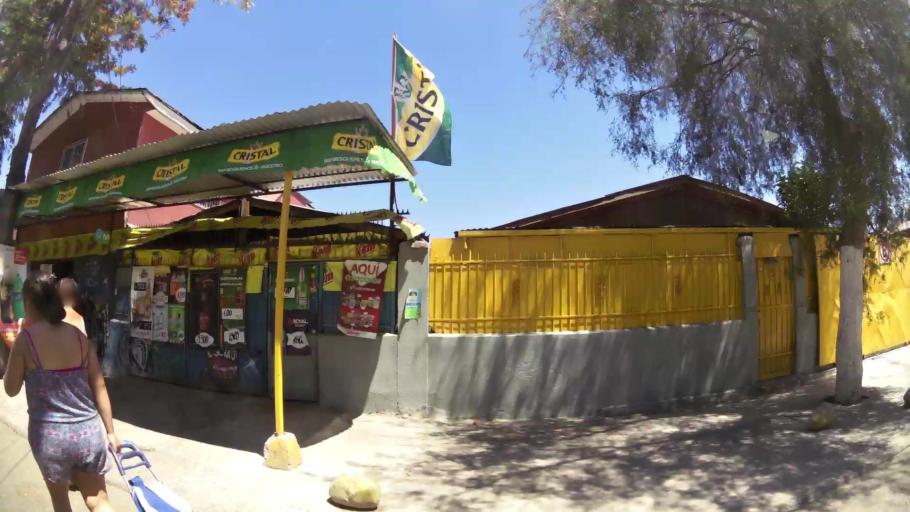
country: CL
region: Santiago Metropolitan
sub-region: Provincia de Santiago
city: La Pintana
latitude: -33.5674
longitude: -70.6680
